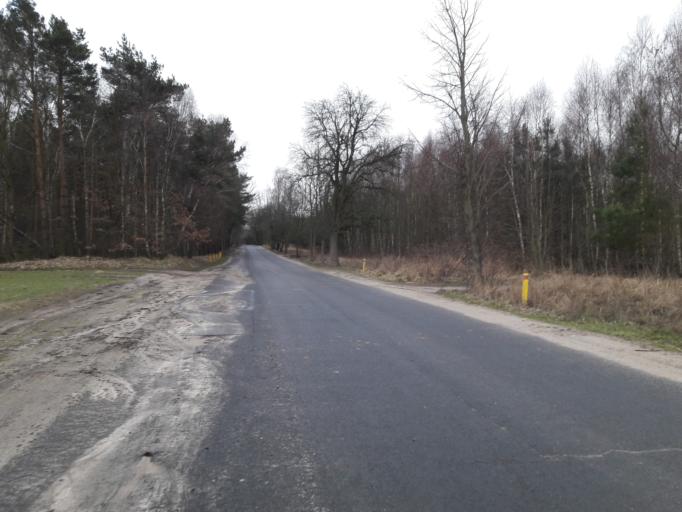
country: PL
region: Greater Poland Voivodeship
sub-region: Powiat poznanski
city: Suchy Las
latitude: 52.4918
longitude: 16.8881
